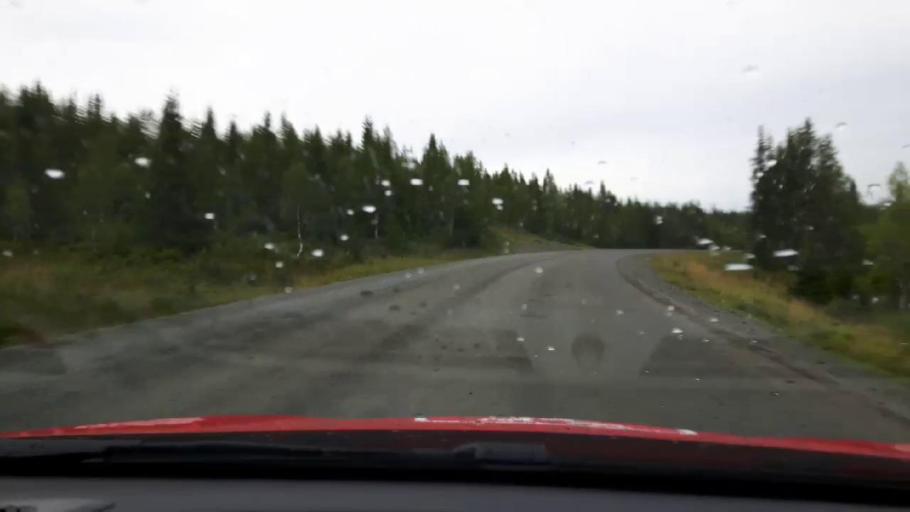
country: SE
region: Jaemtland
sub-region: Are Kommun
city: Are
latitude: 63.4148
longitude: 12.7659
